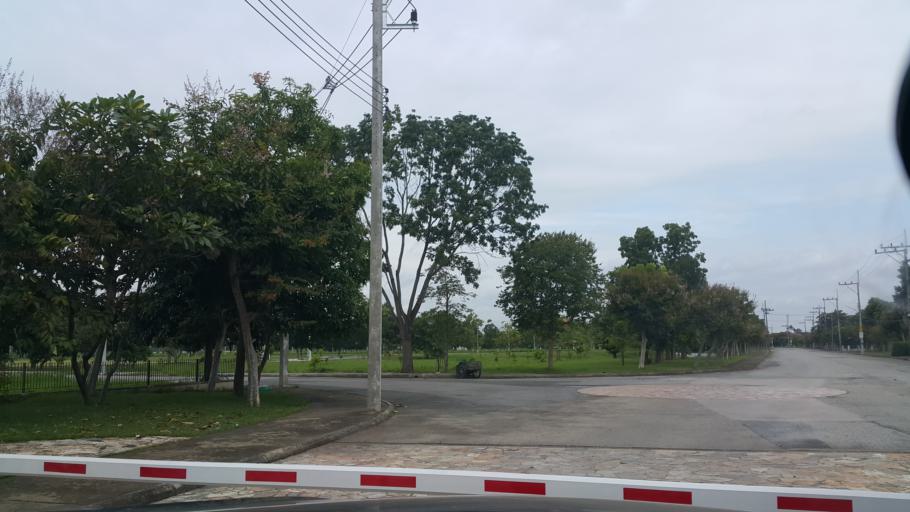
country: TH
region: Chiang Mai
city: San Kamphaeng
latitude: 18.7156
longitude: 99.1384
